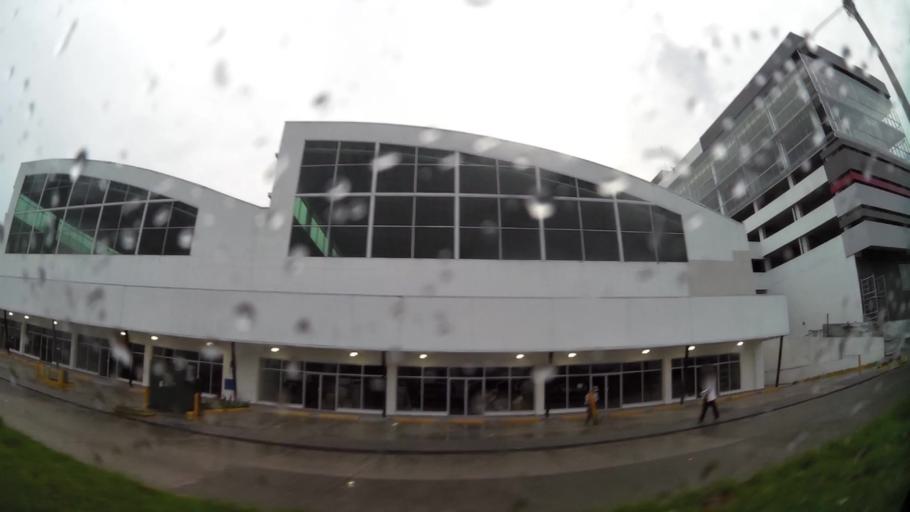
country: PA
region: Panama
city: Panama
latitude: 9.0319
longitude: -79.5319
